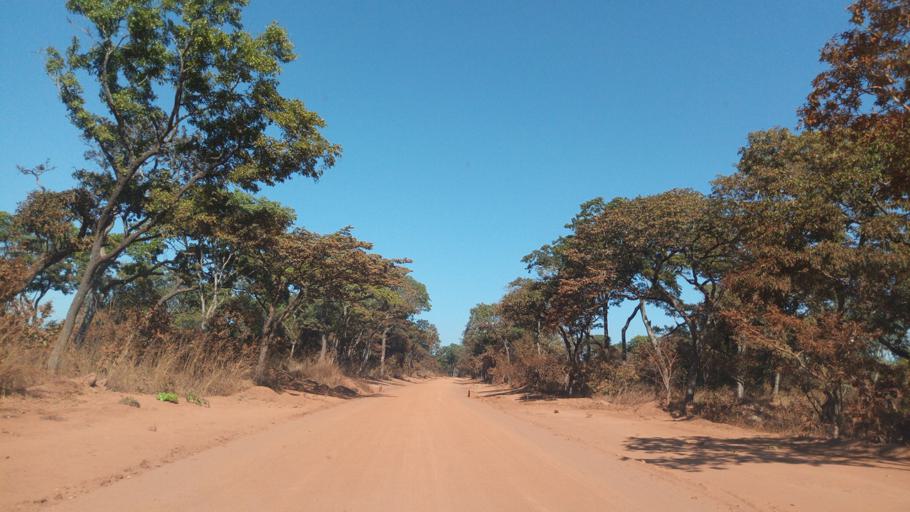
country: ZM
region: Luapula
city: Mwense
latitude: -10.7364
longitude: 28.3395
